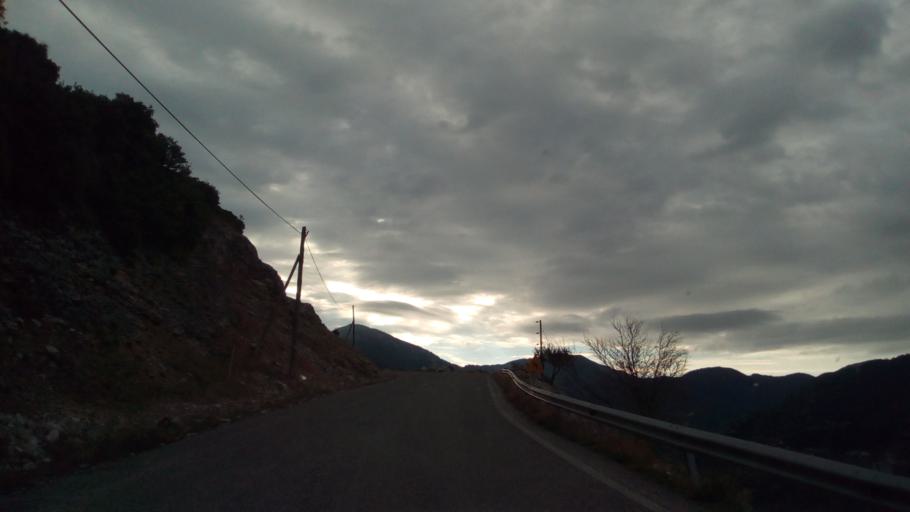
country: GR
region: West Greece
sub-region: Nomos Aitolias kai Akarnanias
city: Thermo
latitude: 38.5916
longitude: 21.8193
